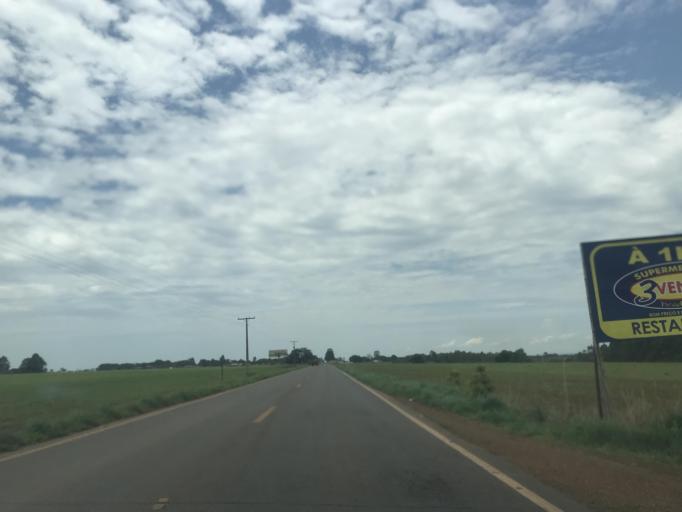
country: BR
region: Goias
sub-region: Luziania
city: Luziania
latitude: -16.3025
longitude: -48.0110
